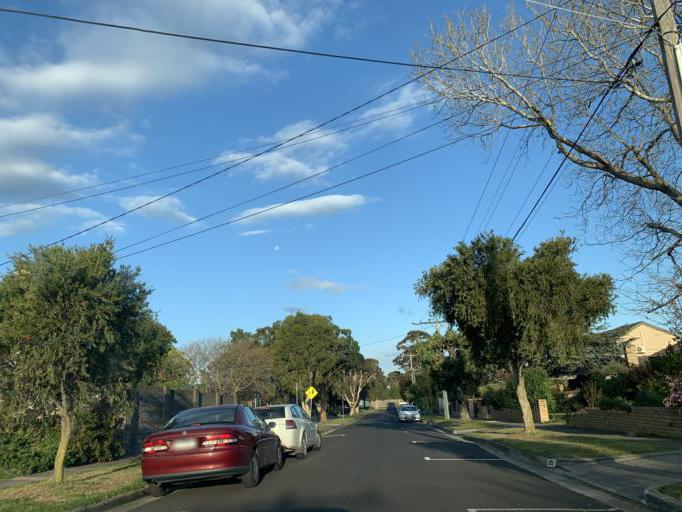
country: AU
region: Victoria
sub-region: Kingston
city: Parkdale
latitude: -37.9827
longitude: 145.0857
